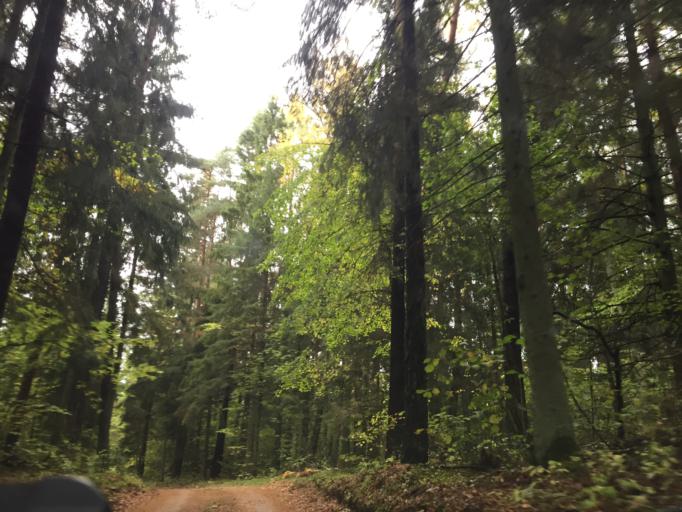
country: LV
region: Auces Novads
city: Auce
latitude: 56.5490
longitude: 23.0369
